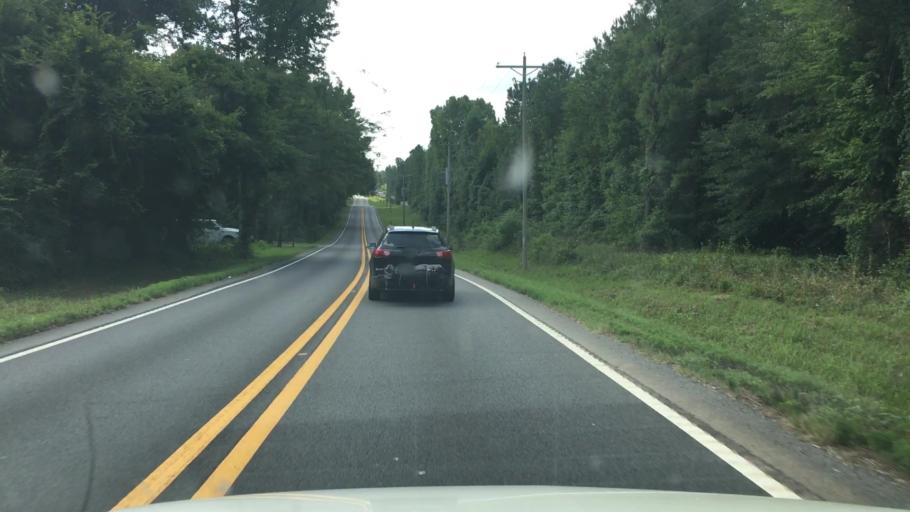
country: US
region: Arkansas
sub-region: Garland County
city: Lake Hamilton
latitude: 34.2727
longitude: -93.1485
